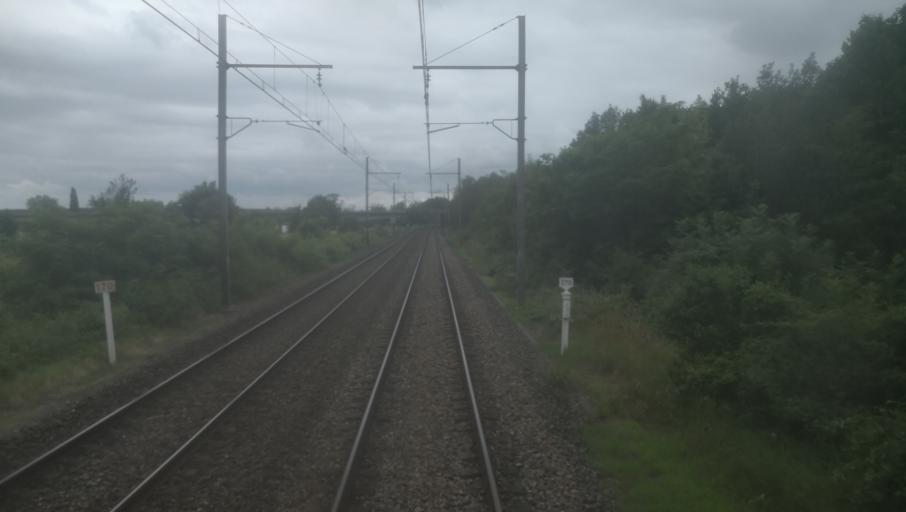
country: FR
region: Midi-Pyrenees
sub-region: Departement du Tarn-et-Garonne
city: Saint-Nicolas-de-la-Grave
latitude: 44.0876
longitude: 0.9884
